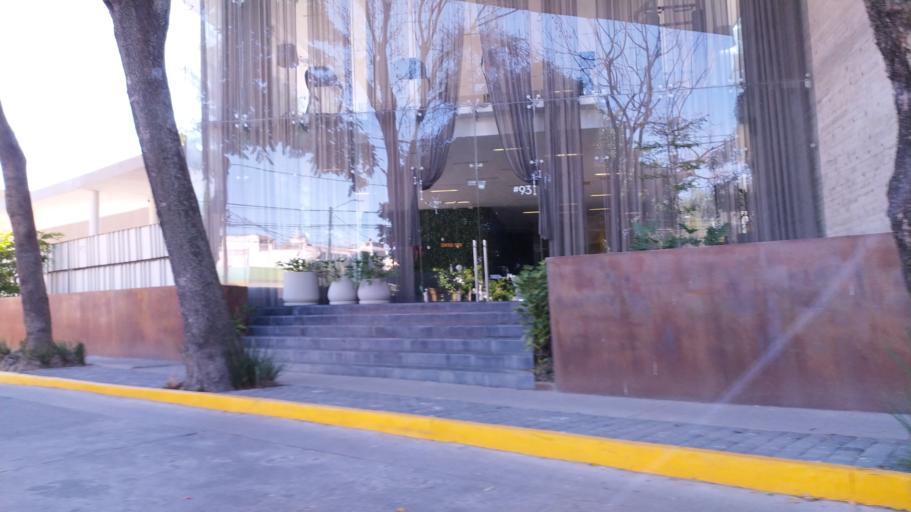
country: MX
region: Jalisco
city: Guadalajara
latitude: 20.6765
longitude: -103.4010
